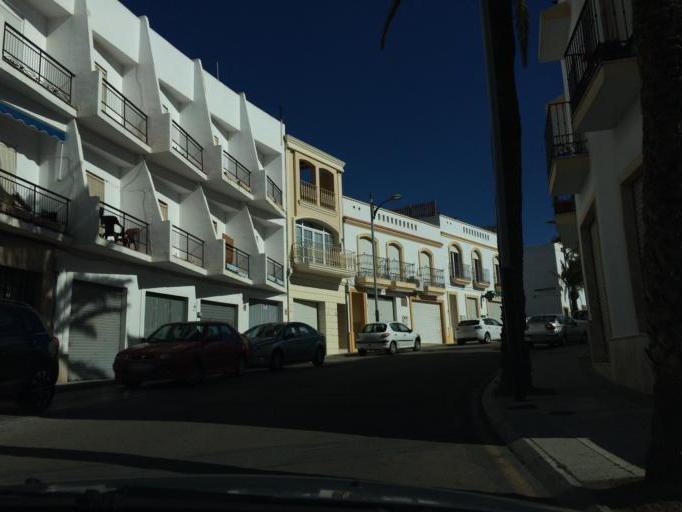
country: ES
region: Andalusia
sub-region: Provincia de Almeria
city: Nijar
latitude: 36.9655
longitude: -2.2084
